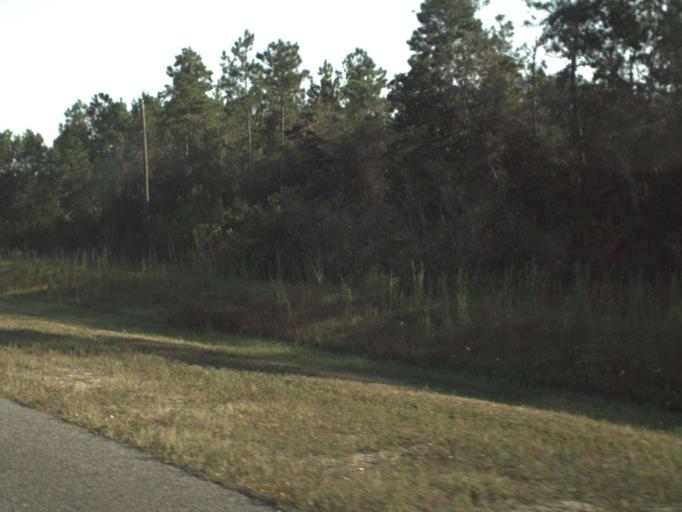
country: US
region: Florida
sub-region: Bay County
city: Laguna Beach
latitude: 30.3391
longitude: -85.8587
